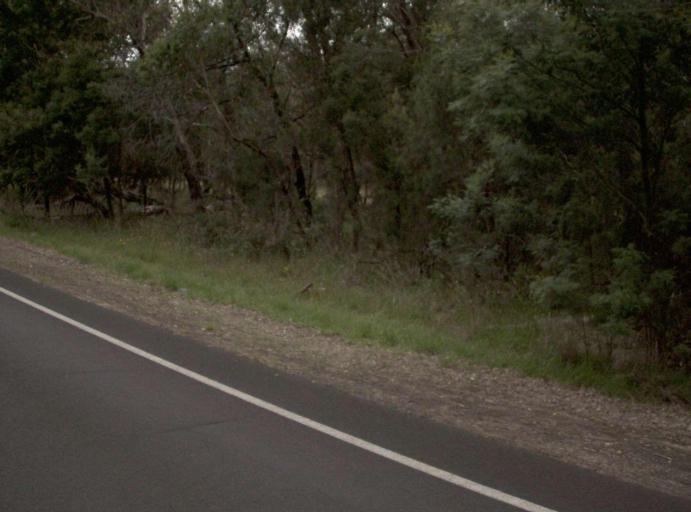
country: AU
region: Victoria
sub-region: Wellington
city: Sale
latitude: -38.4133
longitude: 146.9622
